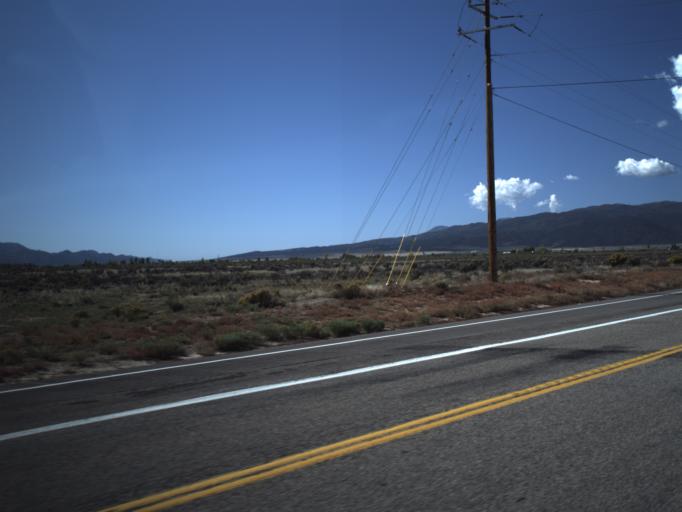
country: US
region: Utah
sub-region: Iron County
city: Cedar City
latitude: 37.6812
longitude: -113.1698
